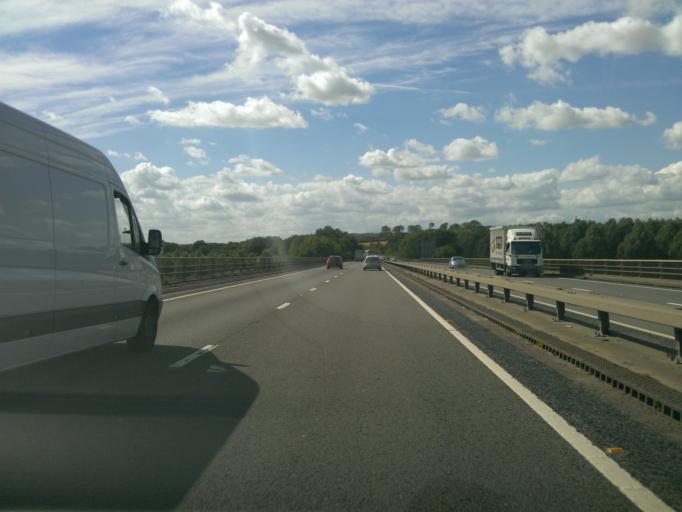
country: GB
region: England
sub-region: Northamptonshire
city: Thrapston
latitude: 52.3896
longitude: -0.5405
